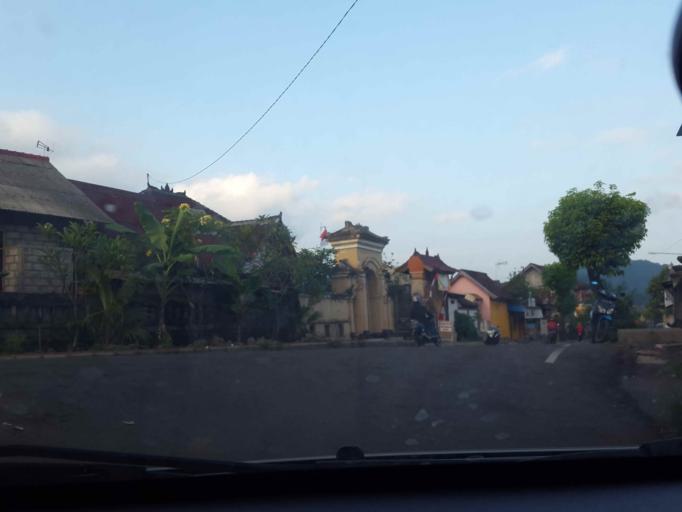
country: ID
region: Bali
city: Semarapura
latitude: -8.5445
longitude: 115.4168
